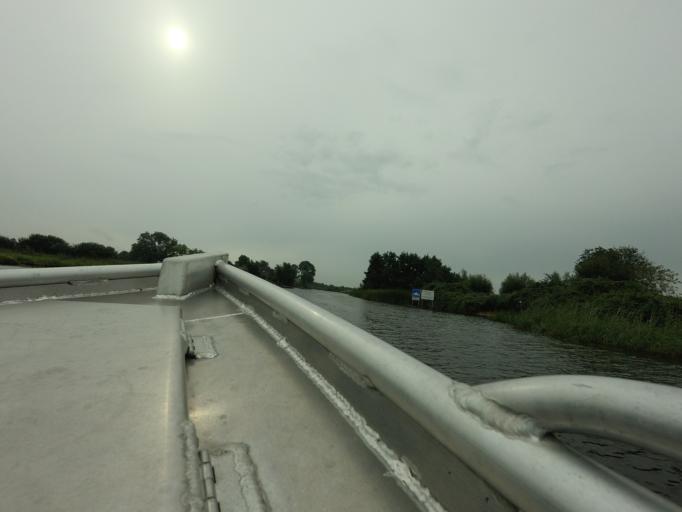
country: NL
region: Overijssel
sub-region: Gemeente Steenwijkerland
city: Sint Jansklooster
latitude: 52.7209
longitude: 6.0157
